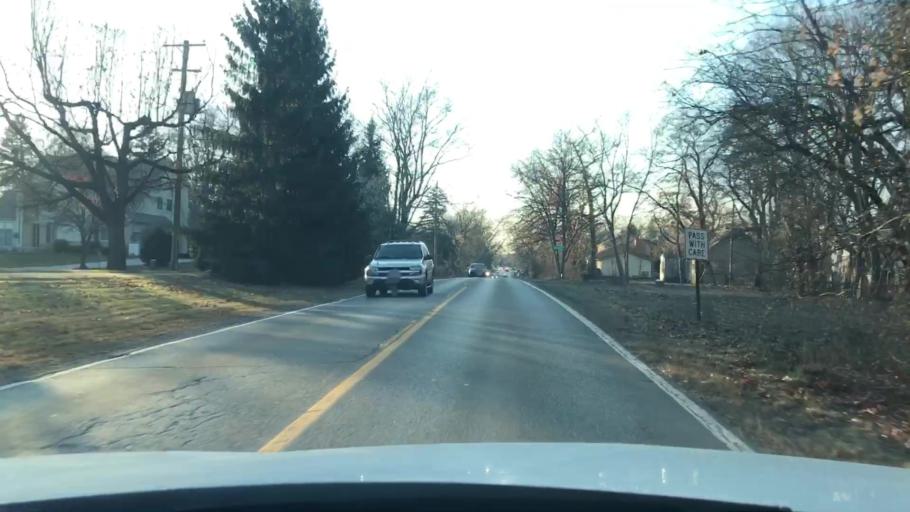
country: US
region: Michigan
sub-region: Oakland County
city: Wolverine Lake
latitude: 42.5990
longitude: -83.4400
